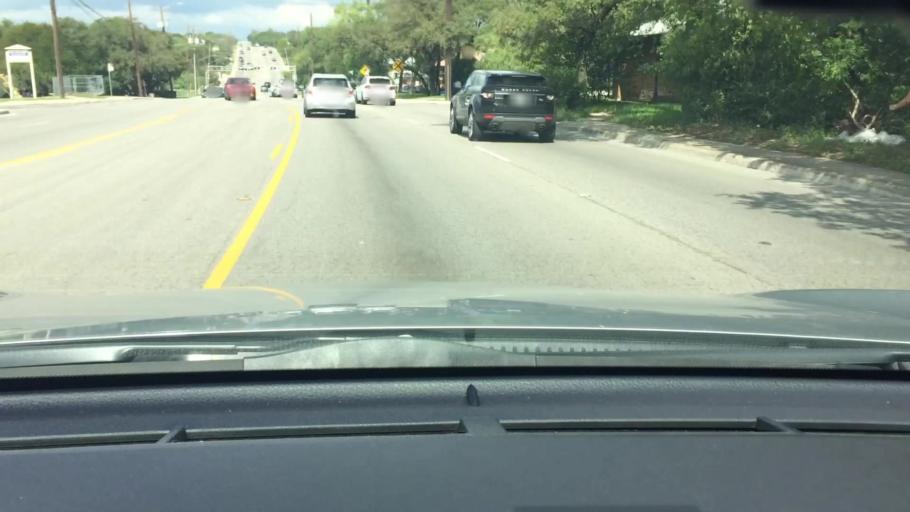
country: US
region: Texas
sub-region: Bexar County
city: Shavano Park
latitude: 29.5542
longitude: -98.5686
